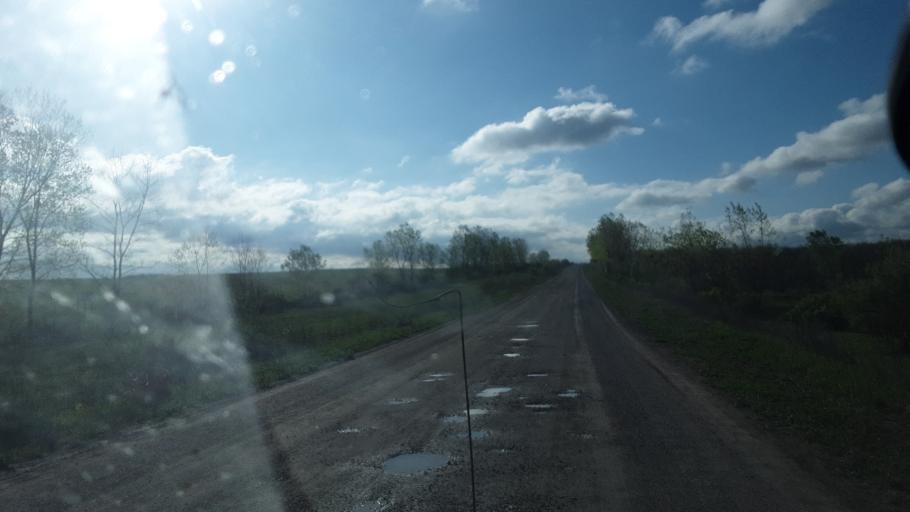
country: US
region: Ohio
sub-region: Noble County
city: Caldwell
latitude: 39.8041
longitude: -81.6433
